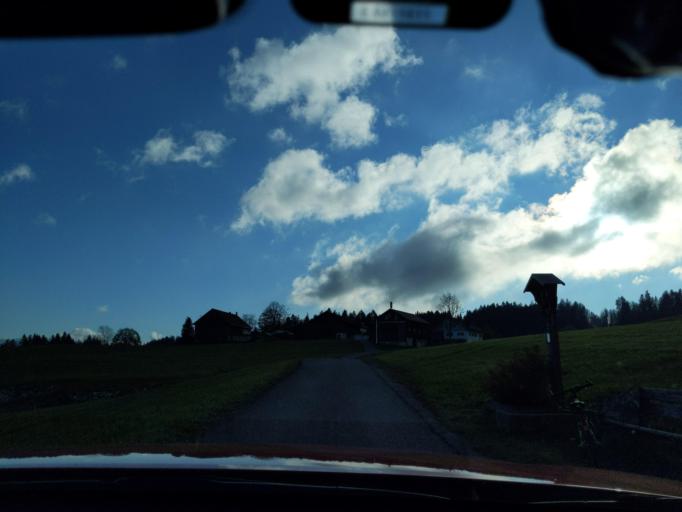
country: AT
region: Vorarlberg
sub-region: Politischer Bezirk Bregenz
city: Eichenberg
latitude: 47.5239
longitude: 9.7922
